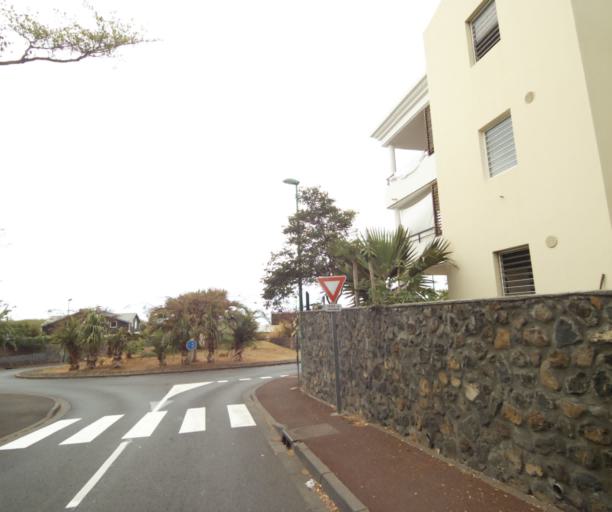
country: RE
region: Reunion
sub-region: Reunion
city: Saint-Paul
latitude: -21.0652
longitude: 55.2293
